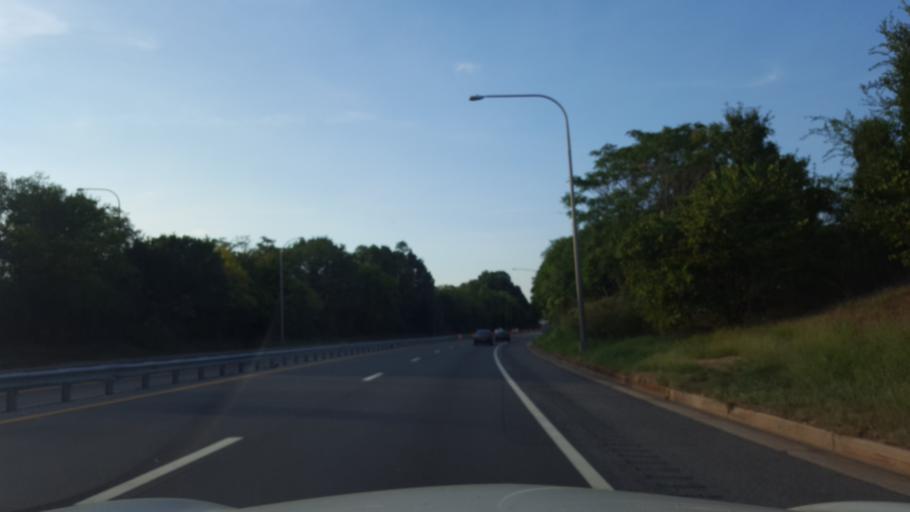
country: US
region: Delaware
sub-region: New Castle County
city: Newport
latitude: 39.7215
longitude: -75.6151
